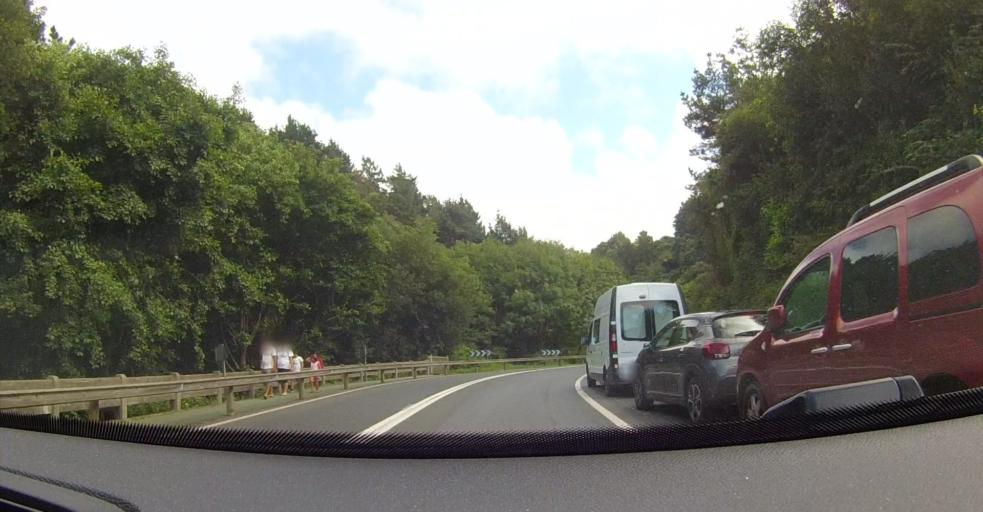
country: ES
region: Basque Country
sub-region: Bizkaia
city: Elantxobe
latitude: 43.4062
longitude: -2.6531
